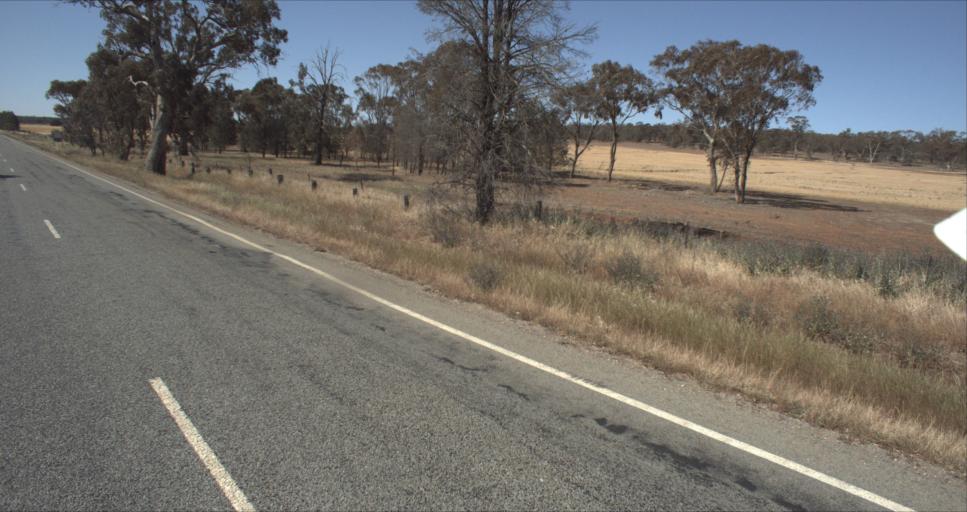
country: AU
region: New South Wales
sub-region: Leeton
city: Leeton
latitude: -34.4574
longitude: 146.4384
